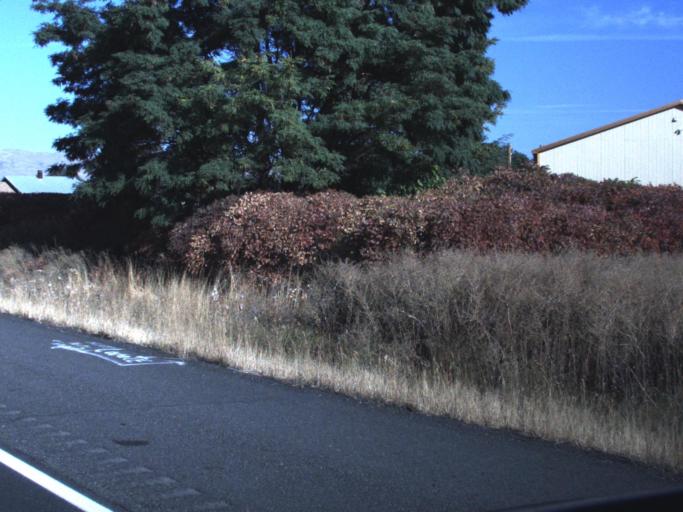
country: US
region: Washington
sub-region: Yakima County
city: Gleed
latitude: 46.6561
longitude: -120.6167
